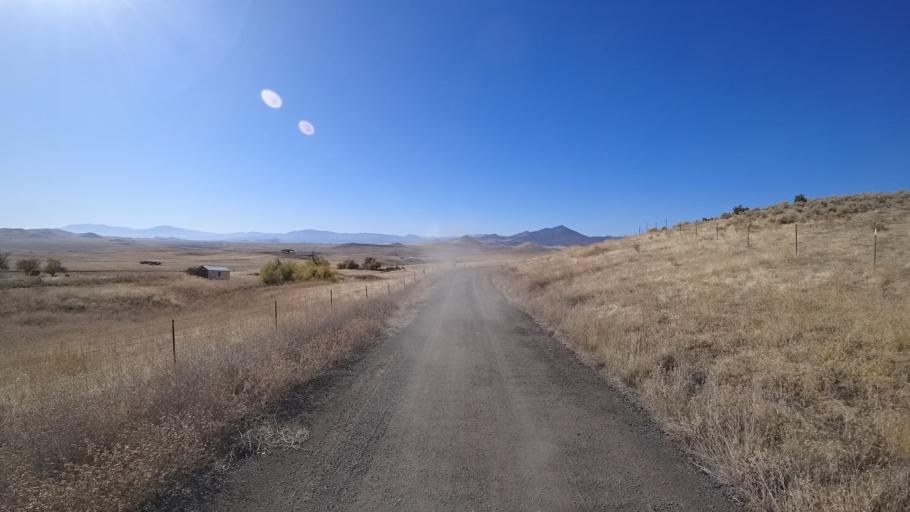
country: US
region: California
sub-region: Siskiyou County
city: Montague
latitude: 41.8445
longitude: -122.4213
